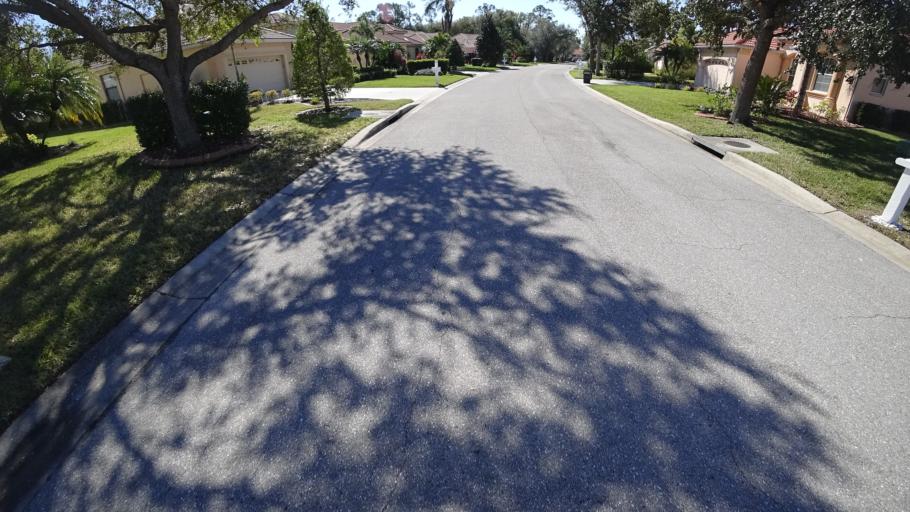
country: US
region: Florida
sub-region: Sarasota County
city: Desoto Lakes
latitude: 27.4294
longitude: -82.4639
